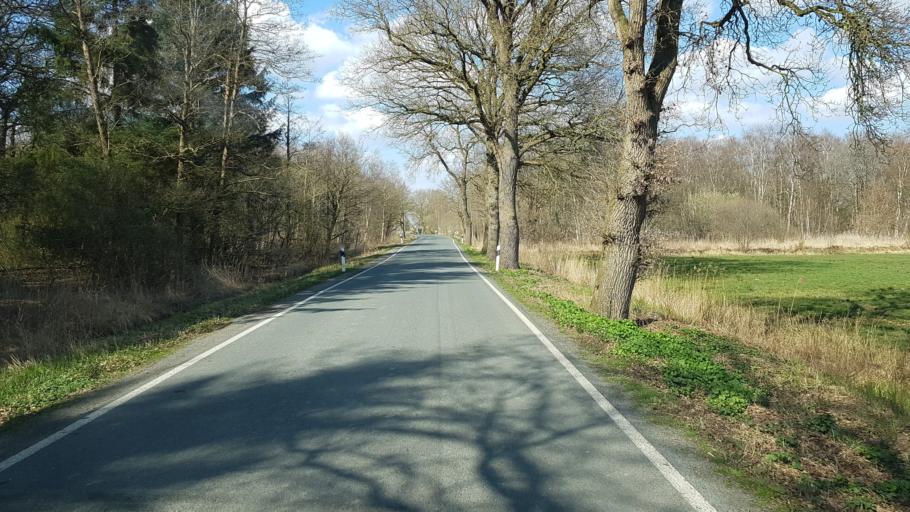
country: DE
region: Lower Saxony
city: Rastede
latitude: 53.3314
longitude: 8.2263
